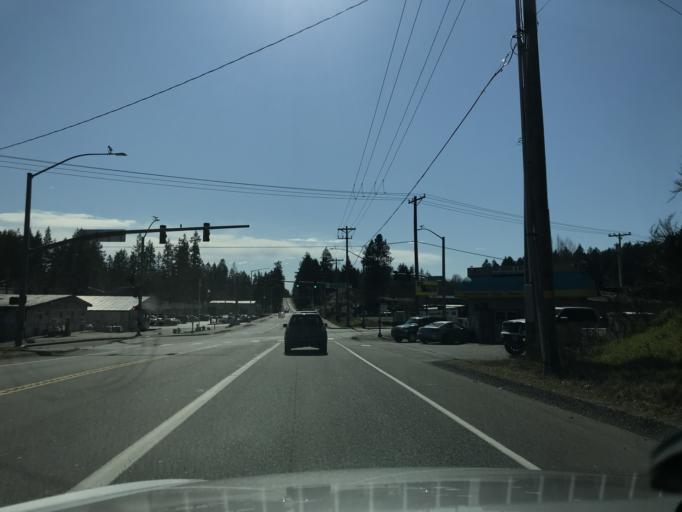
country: US
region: Washington
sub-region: Pierce County
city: Key Center
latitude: 47.3412
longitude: -122.7449
